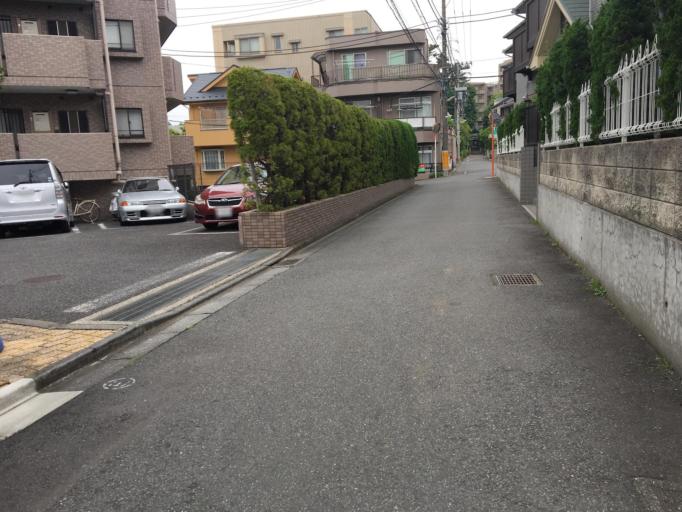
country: JP
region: Tokyo
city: Chofugaoka
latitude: 35.6599
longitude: 139.5691
